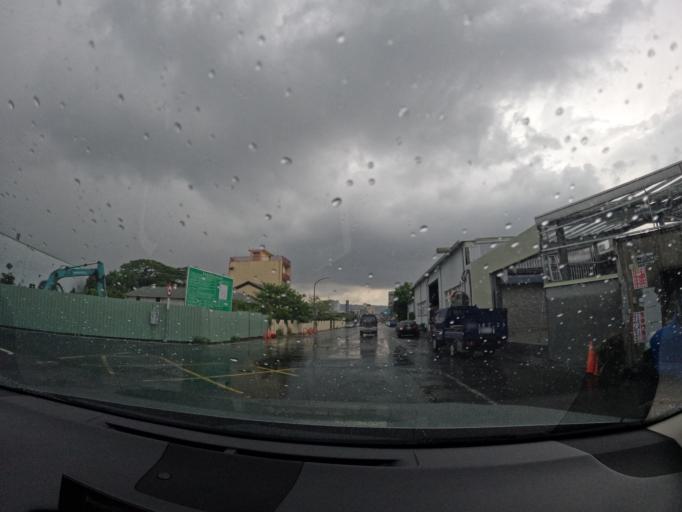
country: TW
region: Taiwan
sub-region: Nantou
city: Nantou
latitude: 23.9073
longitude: 120.6935
